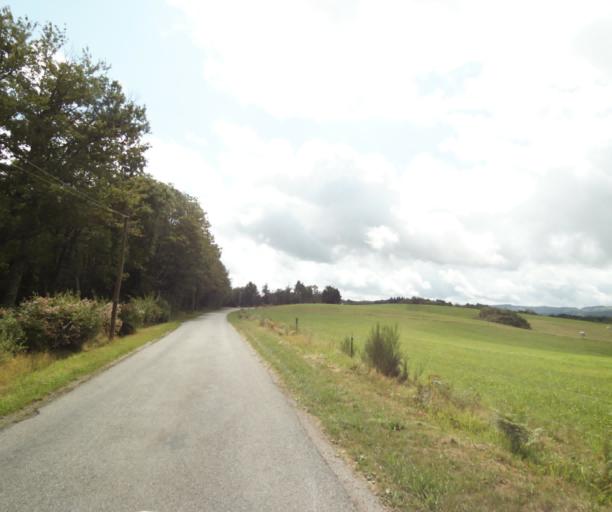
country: FR
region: Limousin
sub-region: Departement de la Correze
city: Sainte-Fortunade
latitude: 45.1755
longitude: 1.8005
